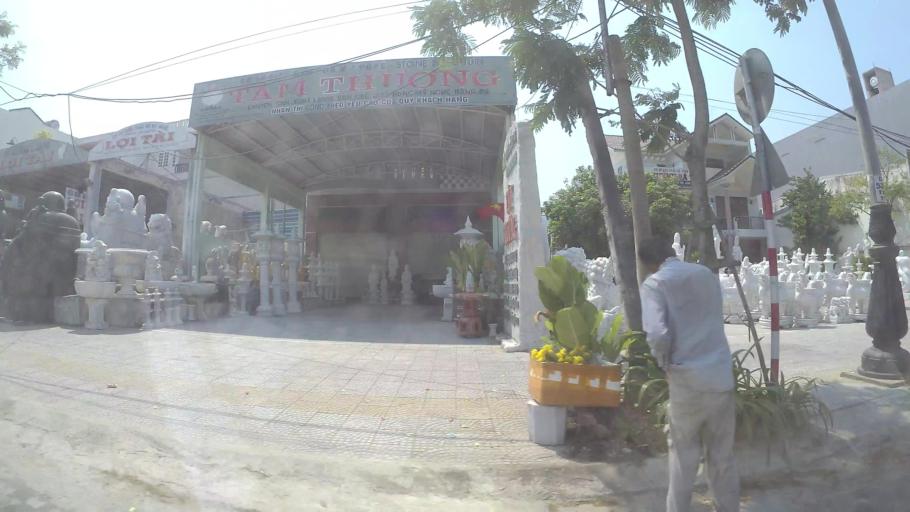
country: VN
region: Da Nang
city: Ngu Hanh Son
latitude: 16.0016
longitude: 108.2671
